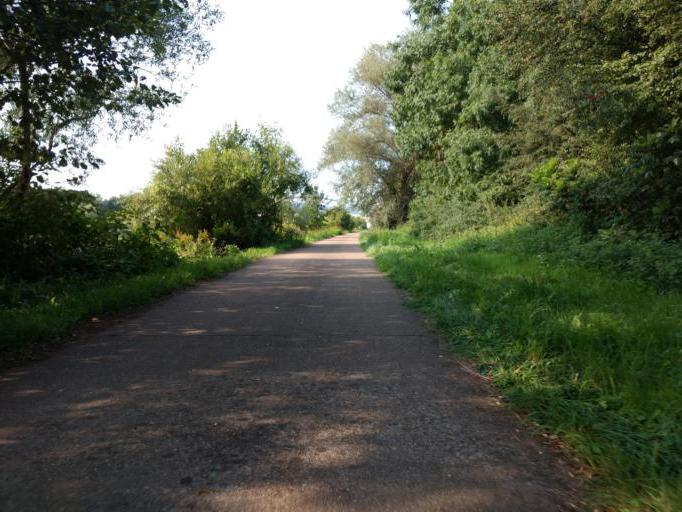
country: DE
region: Saarland
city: Rehlingen-Siersburg
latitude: 49.3611
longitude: 6.6987
